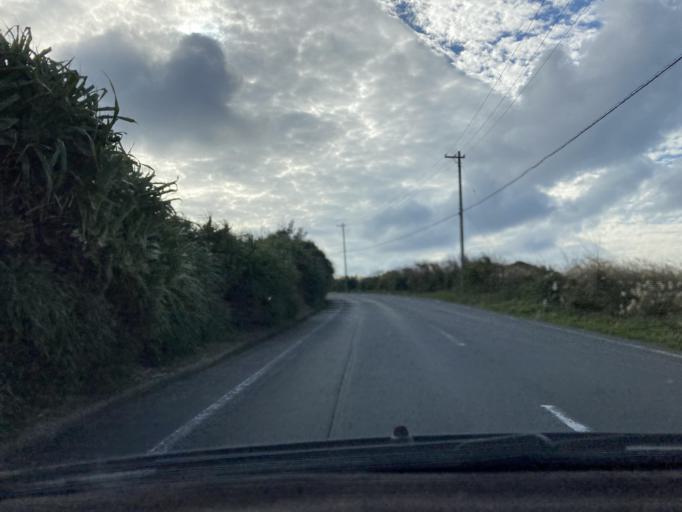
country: JP
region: Okinawa
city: Nago
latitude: 26.8711
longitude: 128.2620
